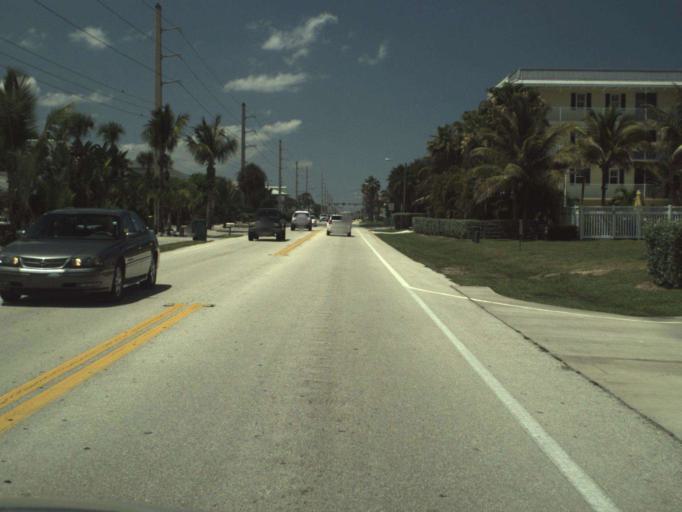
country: US
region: Florida
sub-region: Brevard County
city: Indialantic
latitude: 28.0879
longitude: -80.5655
